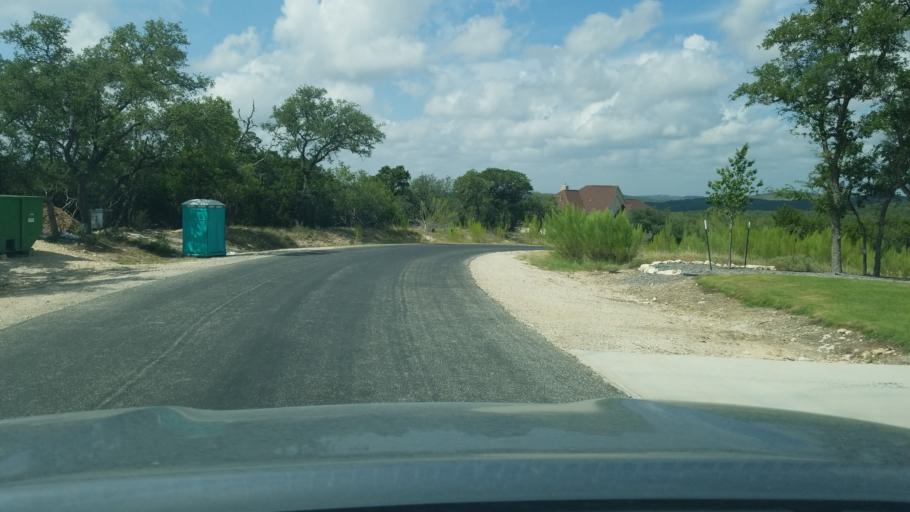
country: US
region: Texas
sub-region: Bexar County
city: Timberwood Park
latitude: 29.6860
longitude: -98.5167
